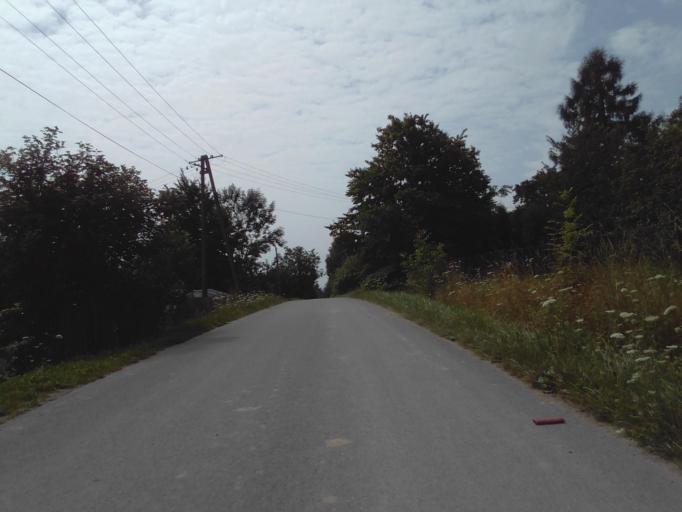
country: PL
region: Subcarpathian Voivodeship
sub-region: Powiat jasielski
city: Kolaczyce
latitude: 49.8253
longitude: 21.4929
